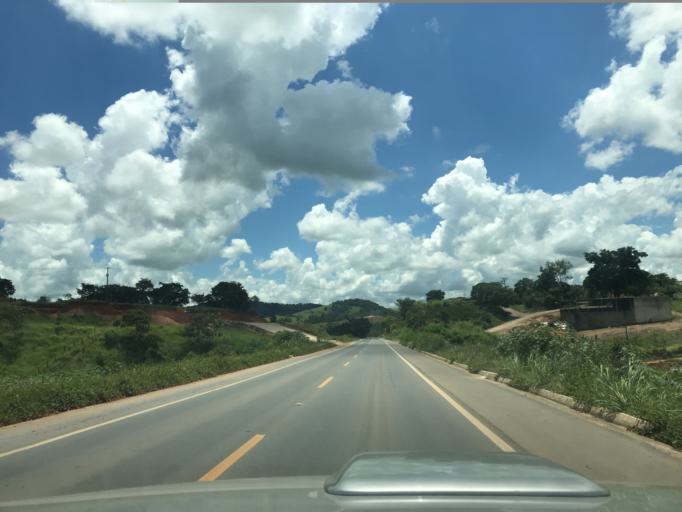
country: BR
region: Minas Gerais
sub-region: Perdoes
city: Perdoes
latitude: -21.1032
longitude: -45.0956
